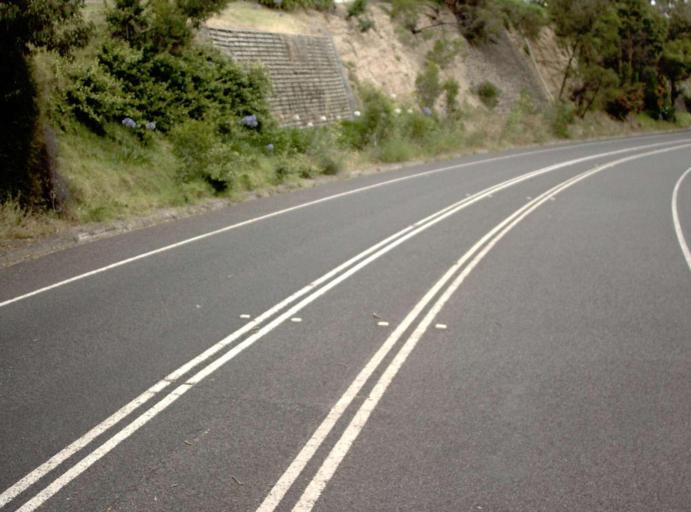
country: AU
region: Victoria
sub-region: Boroondara
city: Kew
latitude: -37.7989
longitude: 145.0215
